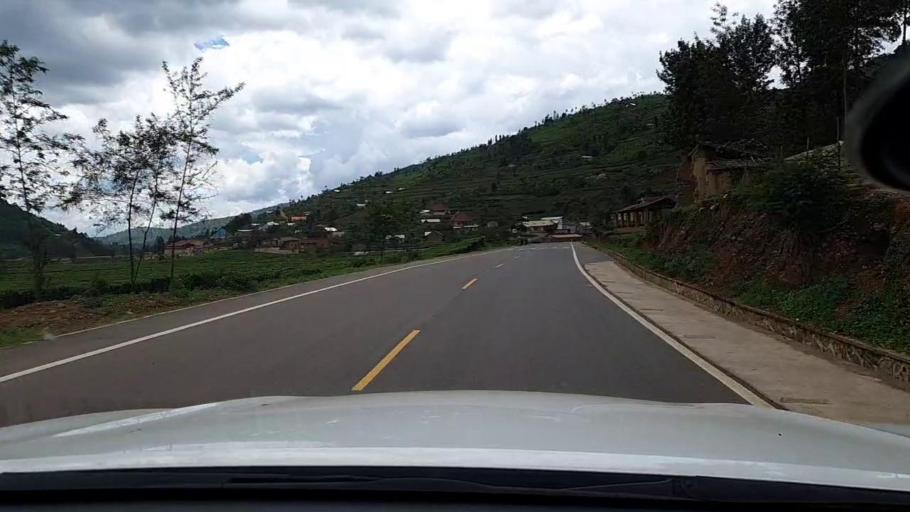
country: RW
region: Northern Province
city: Byumba
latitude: -1.6514
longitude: 29.9029
